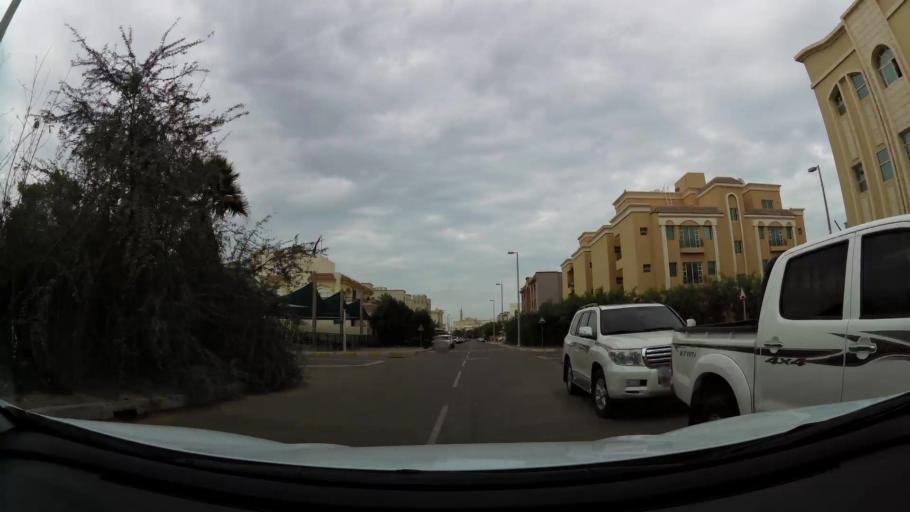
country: AE
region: Abu Dhabi
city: Abu Dhabi
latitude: 24.4377
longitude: 54.4094
